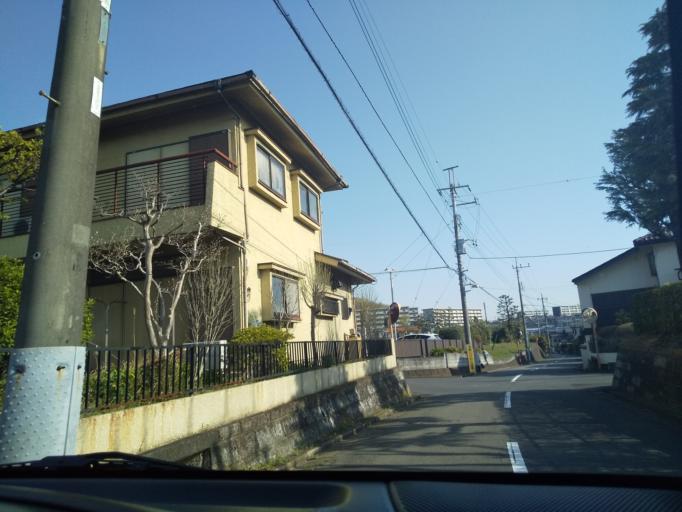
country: JP
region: Tokyo
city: Hino
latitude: 35.6489
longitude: 139.4210
